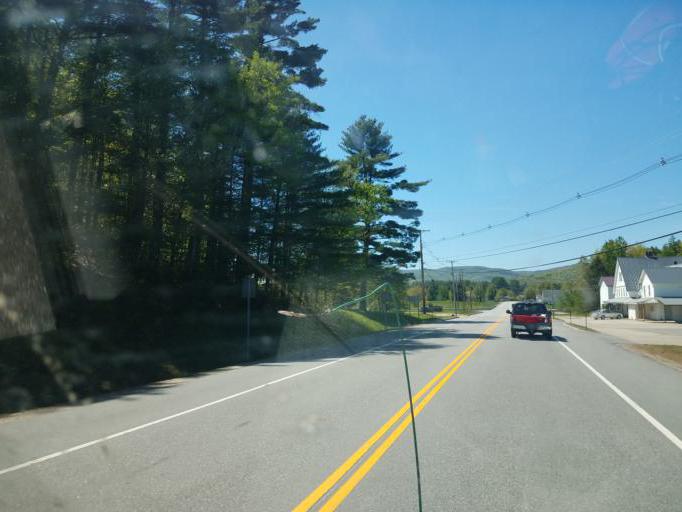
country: US
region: New Hampshire
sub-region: Grafton County
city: Rumney
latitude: 43.8191
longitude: -71.8825
